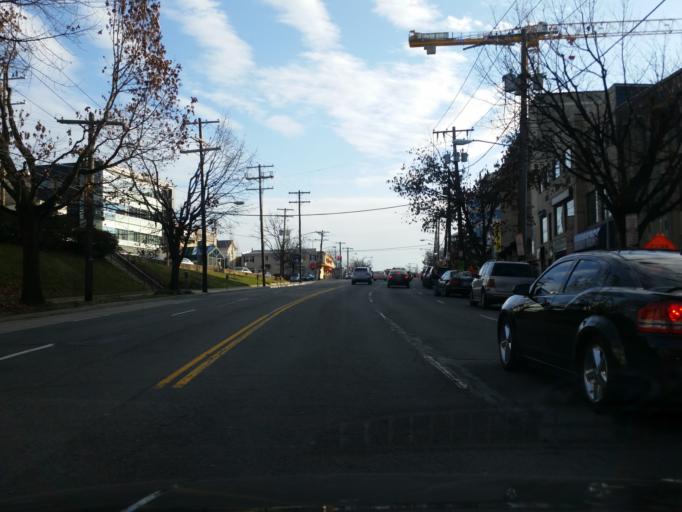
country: US
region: Maryland
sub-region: Montgomery County
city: Friendship Village
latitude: 38.9511
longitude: -77.0808
